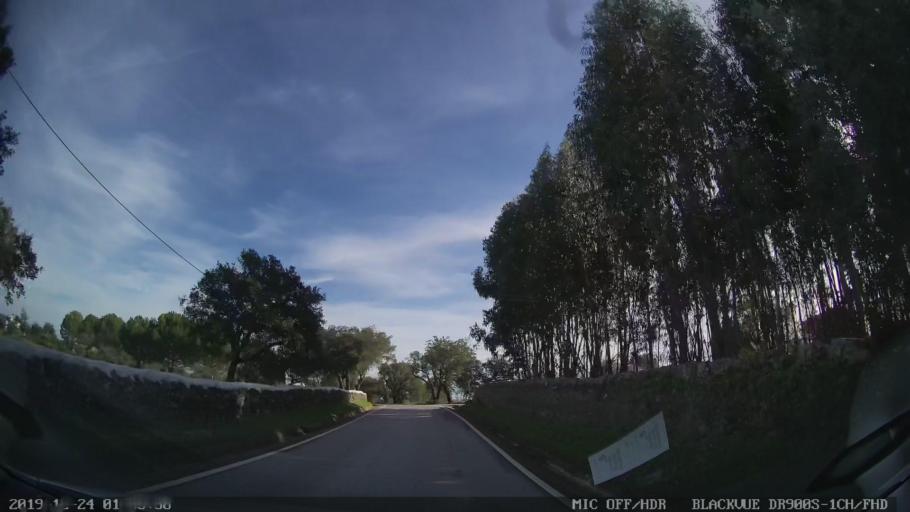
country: PT
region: Portalegre
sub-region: Nisa
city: Nisa
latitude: 39.4854
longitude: -7.7325
